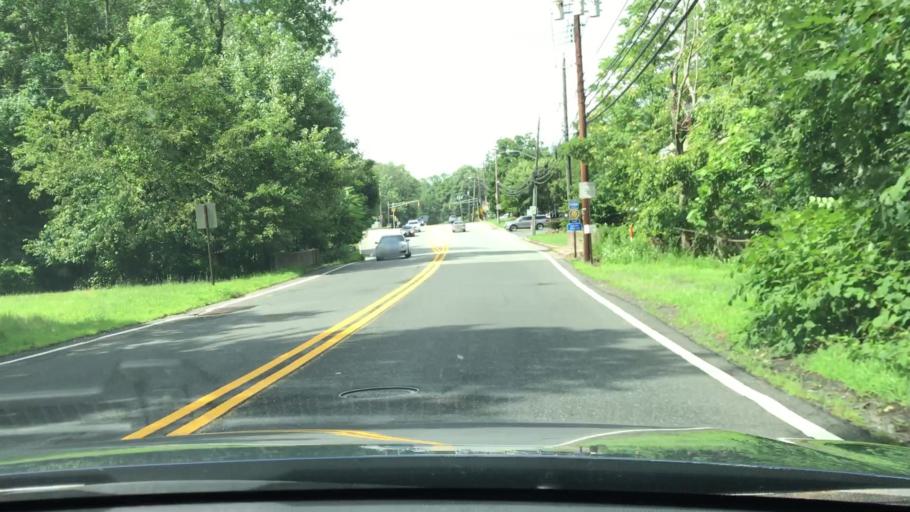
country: US
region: New Jersey
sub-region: Bergen County
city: Wyckoff
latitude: 41.0233
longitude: -74.1675
